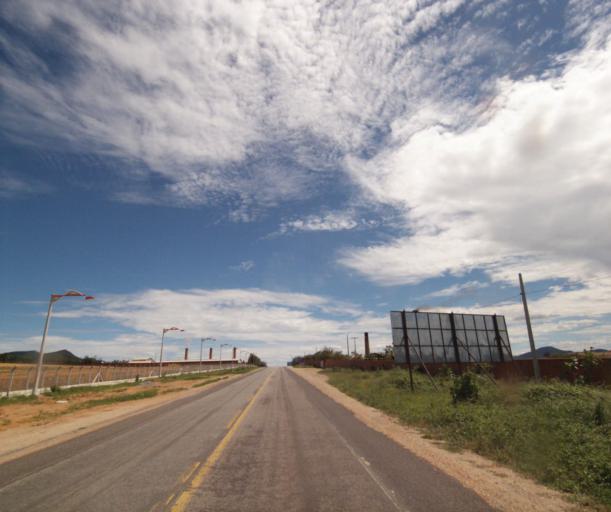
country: BR
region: Bahia
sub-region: Guanambi
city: Guanambi
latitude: -14.2604
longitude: -42.7824
